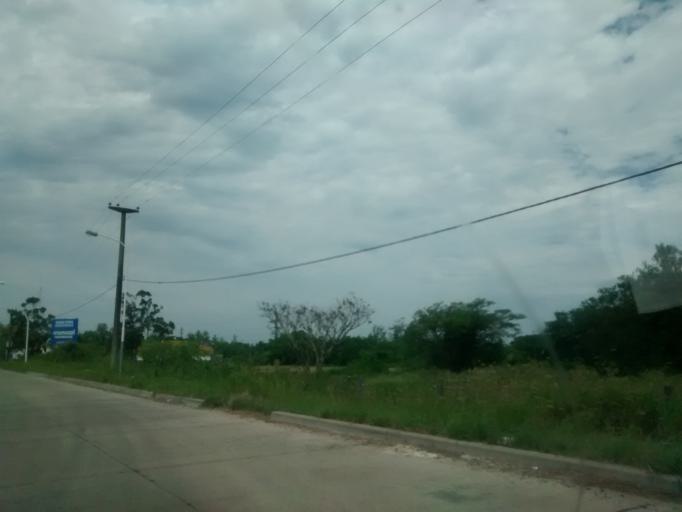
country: AR
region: Chaco
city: Fontana
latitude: -27.4113
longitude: -58.9918
